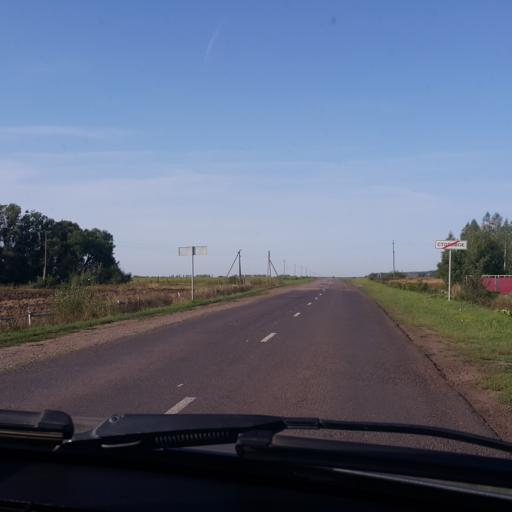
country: RU
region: Tambov
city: Novaya Lyada
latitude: 52.7698
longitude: 41.7443
